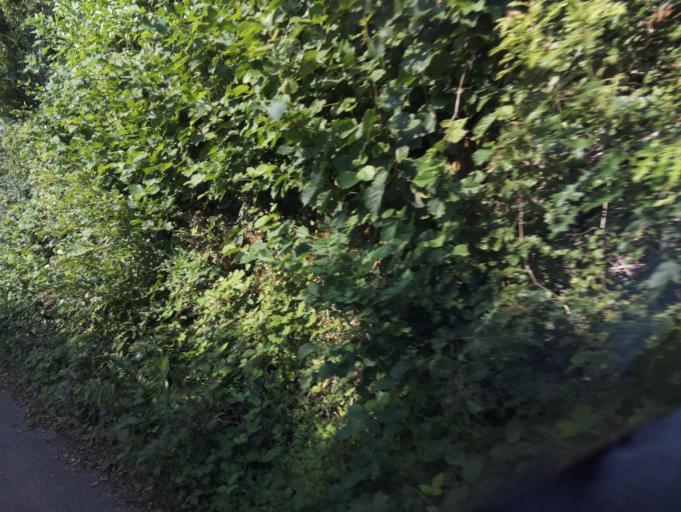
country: GB
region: England
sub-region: Devon
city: Totnes
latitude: 50.4207
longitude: -3.7230
